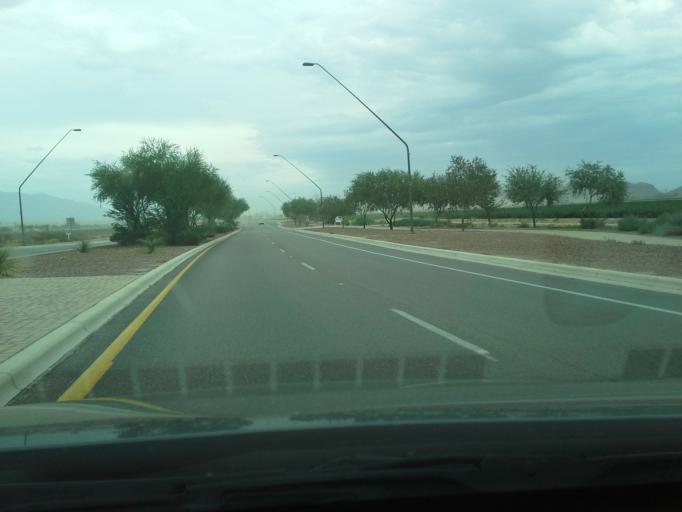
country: US
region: Arizona
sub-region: Pima County
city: Marana
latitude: 32.4243
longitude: -111.1715
